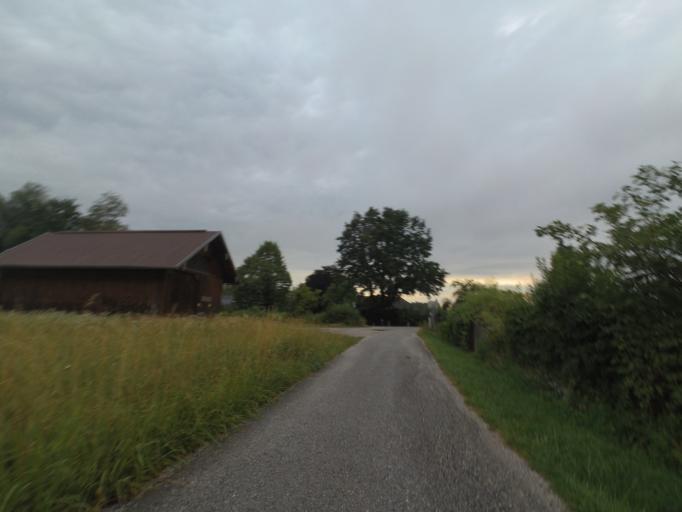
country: AT
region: Salzburg
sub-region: Salzburg Stadt
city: Salzburg
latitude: 47.7678
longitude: 13.0354
